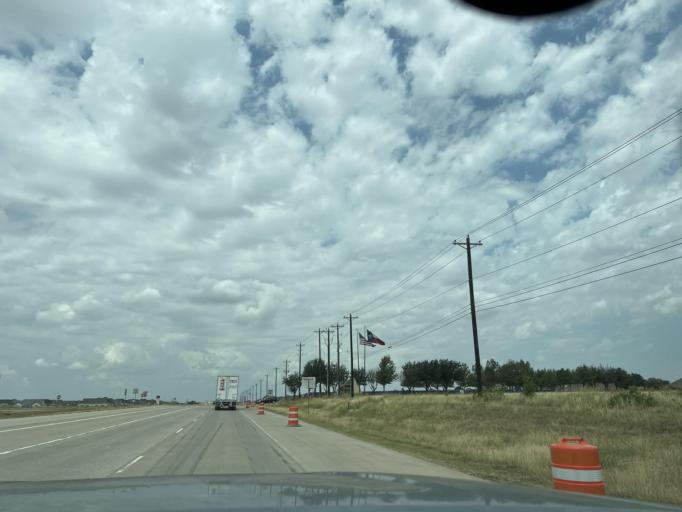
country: US
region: Texas
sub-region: Denton County
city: Justin
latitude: 33.0354
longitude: -97.3285
